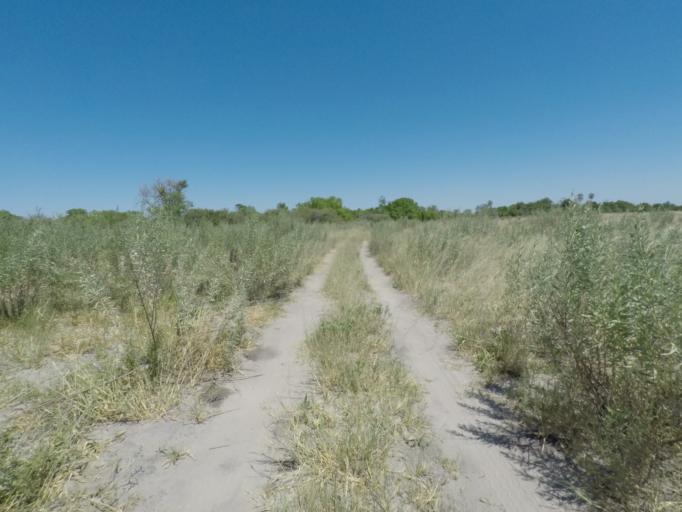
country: BW
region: North West
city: Maun
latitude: -19.4745
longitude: 23.5532
